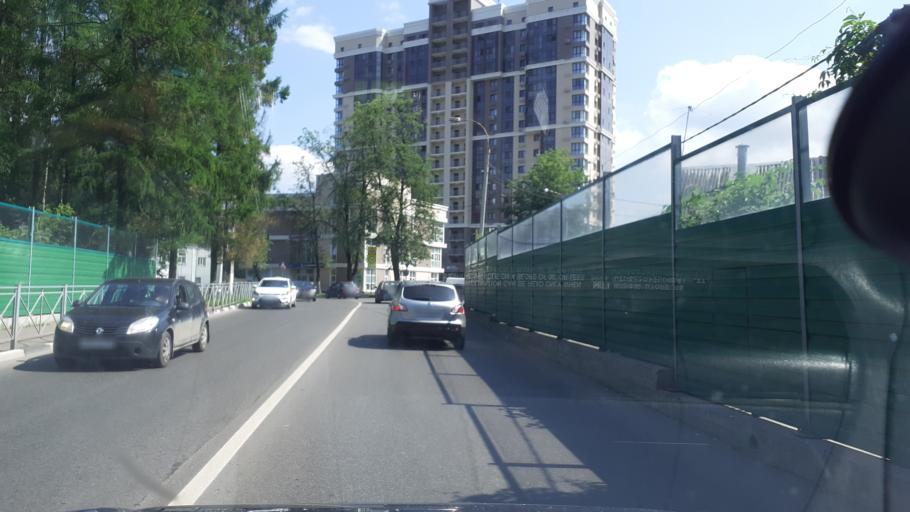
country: RU
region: Moskovskaya
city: Naro-Fominsk
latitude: 55.3861
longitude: 36.7399
